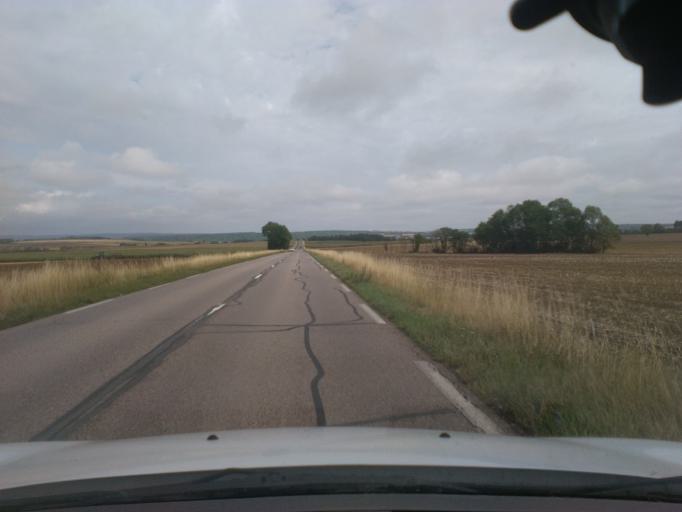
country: FR
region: Lorraine
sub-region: Departement de Meurthe-et-Moselle
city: Pulligny
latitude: 48.4948
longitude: 6.1471
